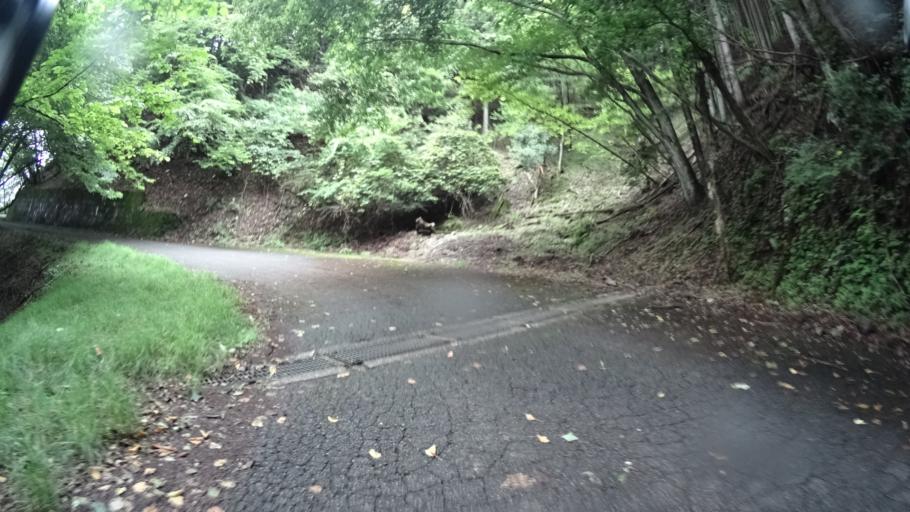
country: JP
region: Saitama
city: Chichibu
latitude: 35.8954
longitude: 139.1242
